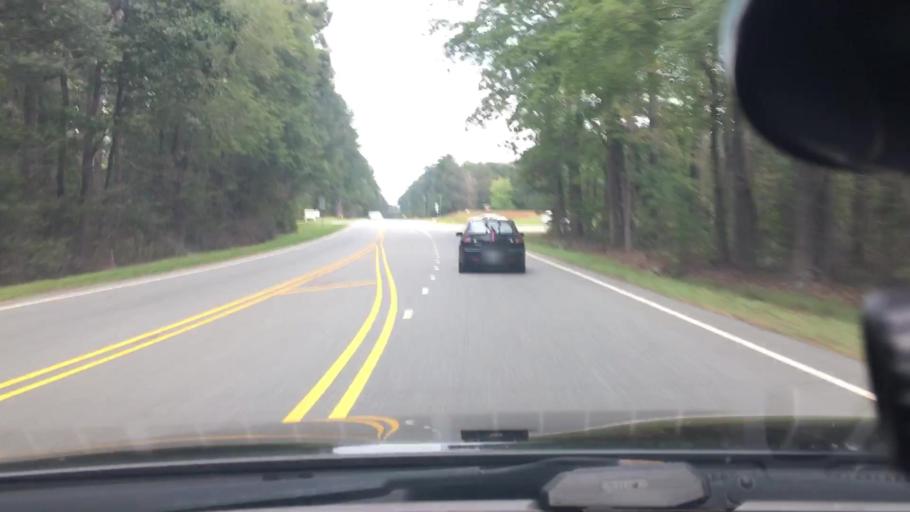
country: US
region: North Carolina
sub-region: Moore County
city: Robbins
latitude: 35.3814
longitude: -79.6593
